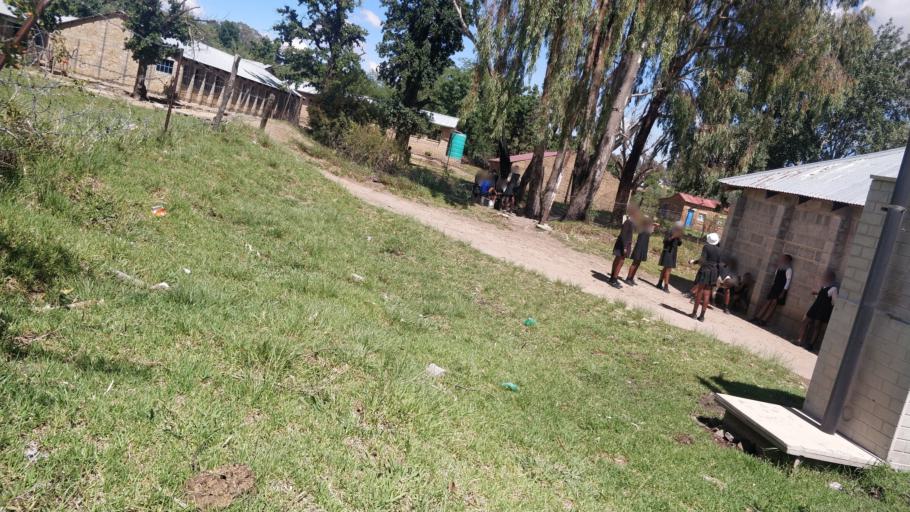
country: LS
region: Maseru
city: Nako
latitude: -29.6291
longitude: 27.5063
